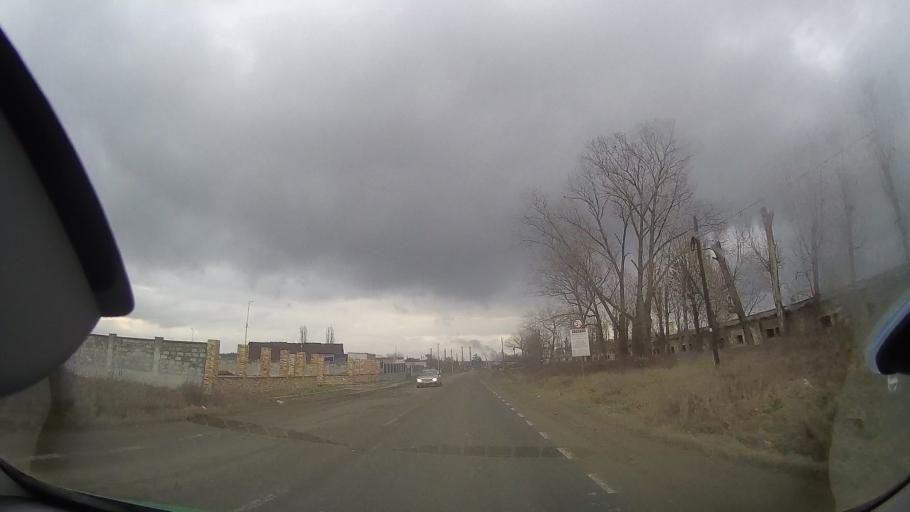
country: RO
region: Cluj
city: Turda
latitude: 46.5459
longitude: 23.7783
